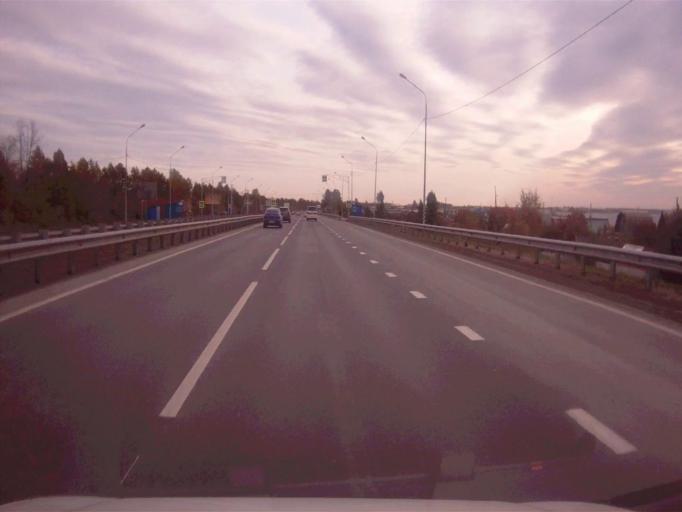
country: RU
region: Chelyabinsk
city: Novosineglazovskiy
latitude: 55.0321
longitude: 61.4449
